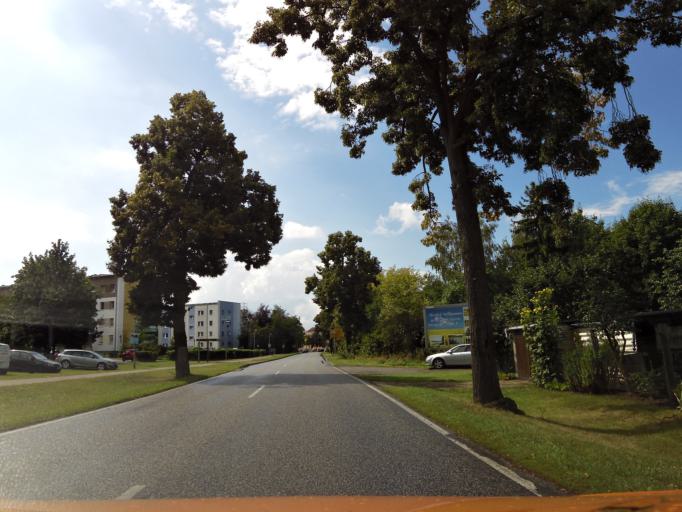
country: DE
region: Brandenburg
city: Ketzin
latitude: 52.4818
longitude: 12.8487
